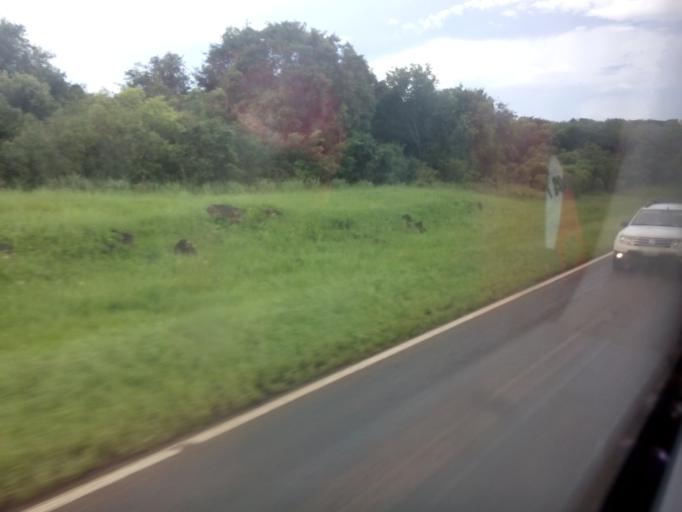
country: AR
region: Misiones
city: Santa Ana
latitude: -27.4233
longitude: -55.6196
